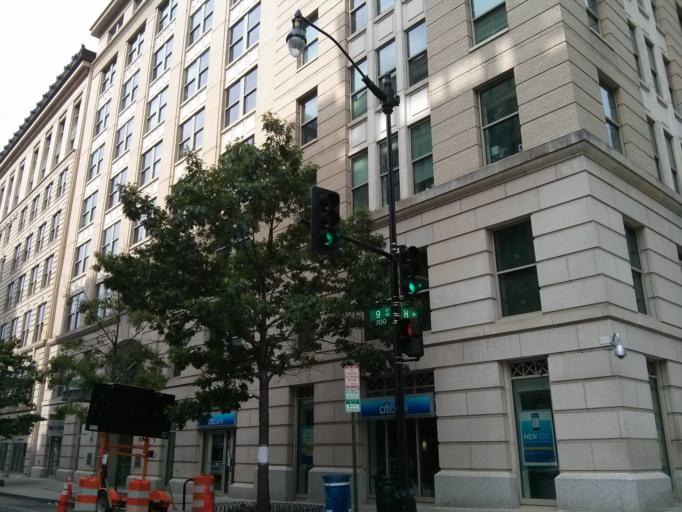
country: US
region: Washington, D.C.
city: Washington, D.C.
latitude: 38.8998
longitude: -77.0241
